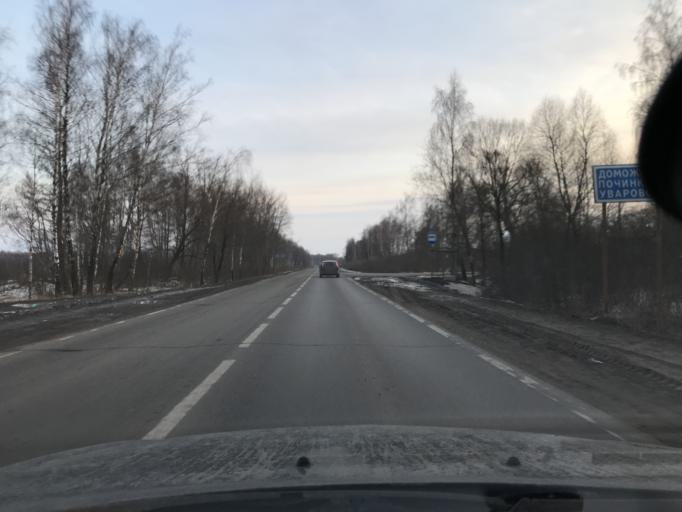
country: RU
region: Kaluga
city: Kaluga
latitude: 54.6116
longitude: 36.2742
